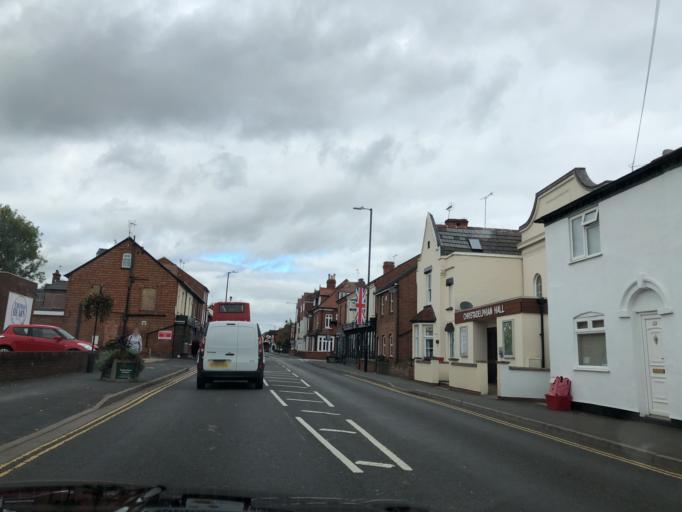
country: GB
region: England
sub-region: Warwickshire
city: Kenilworth
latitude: 52.3393
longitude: -1.5757
